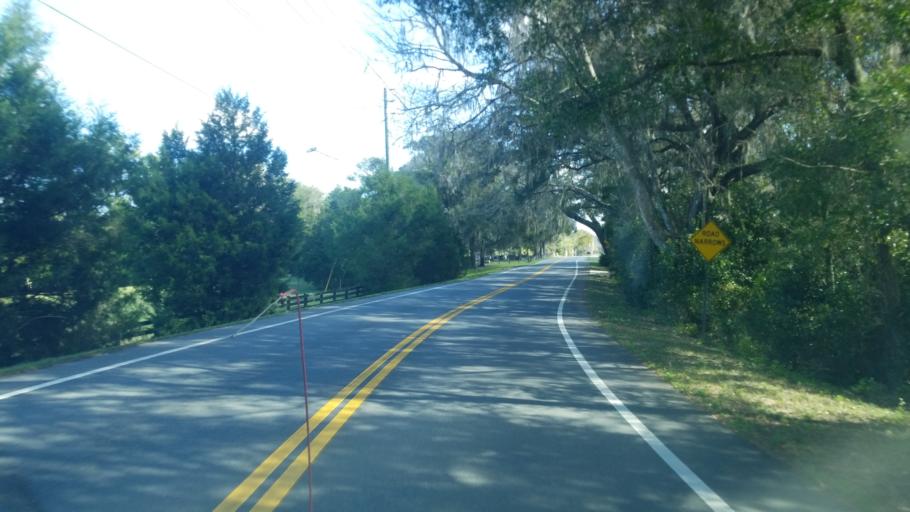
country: US
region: Florida
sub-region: Hernando County
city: North Brooksville
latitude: 28.6350
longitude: -82.3692
